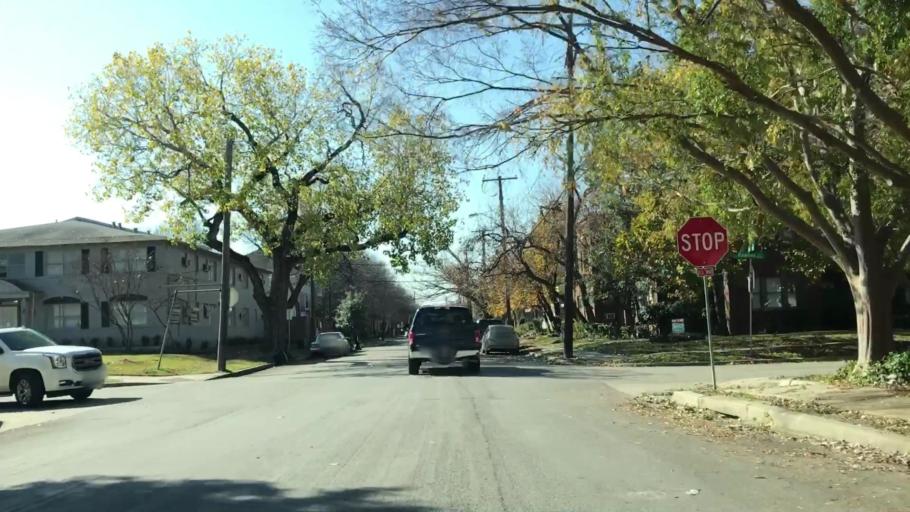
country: US
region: Texas
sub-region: Dallas County
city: Highland Park
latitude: 32.8131
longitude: -96.8087
